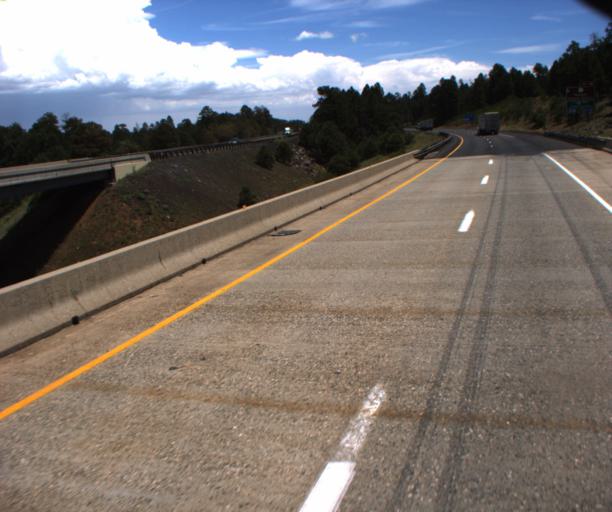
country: US
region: Arizona
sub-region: Coconino County
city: Flagstaff
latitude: 35.1945
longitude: -111.7375
